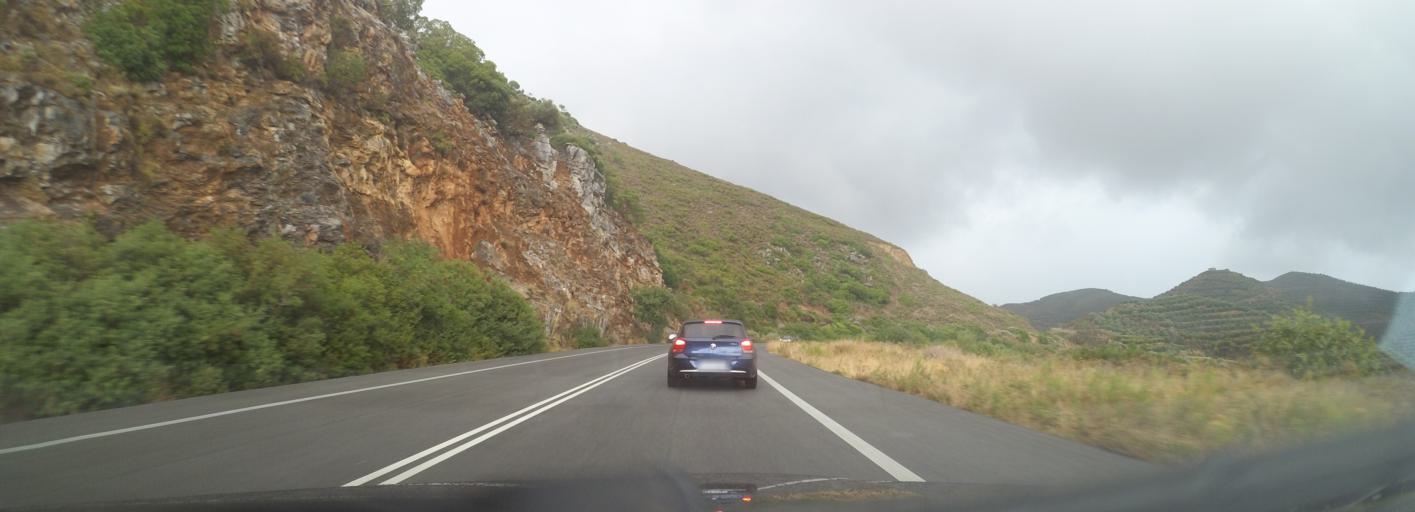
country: GR
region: Crete
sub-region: Nomos Rethymnis
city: Anogeia
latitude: 35.3909
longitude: 24.9023
